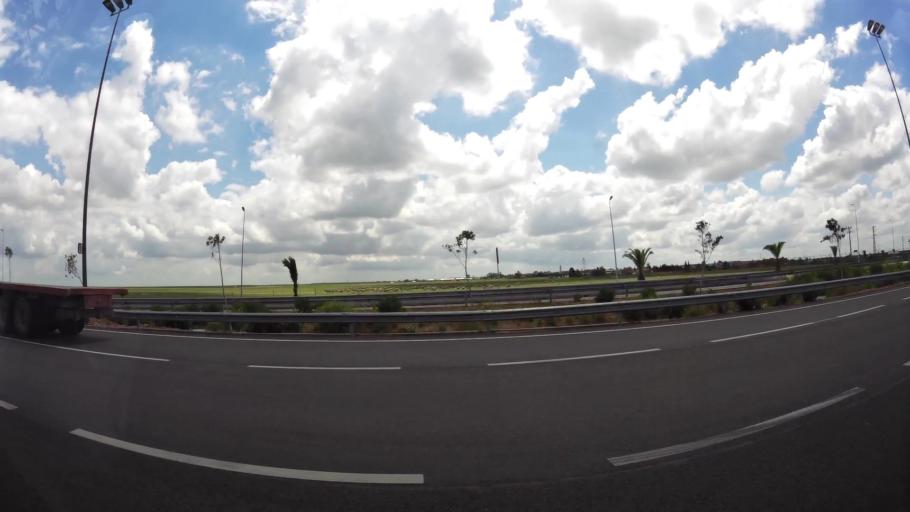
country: MA
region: Chaouia-Ouardigha
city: Nouaseur
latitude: 33.3893
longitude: -7.6154
